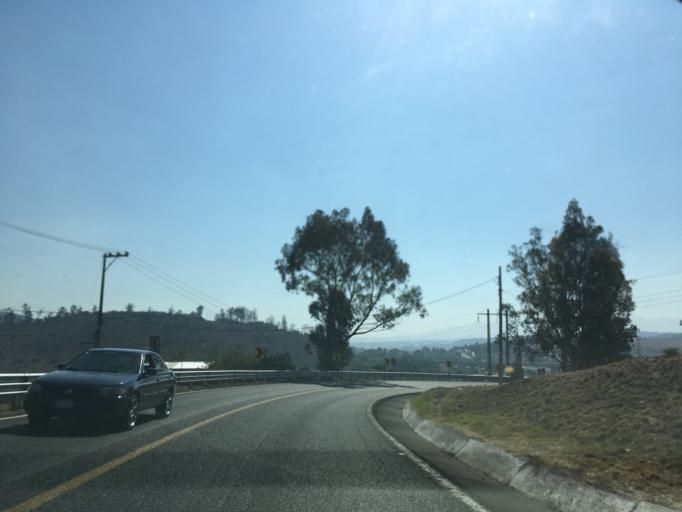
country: MX
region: Michoacan
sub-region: Morelia
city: La Aldea
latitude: 19.7376
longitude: -101.1086
